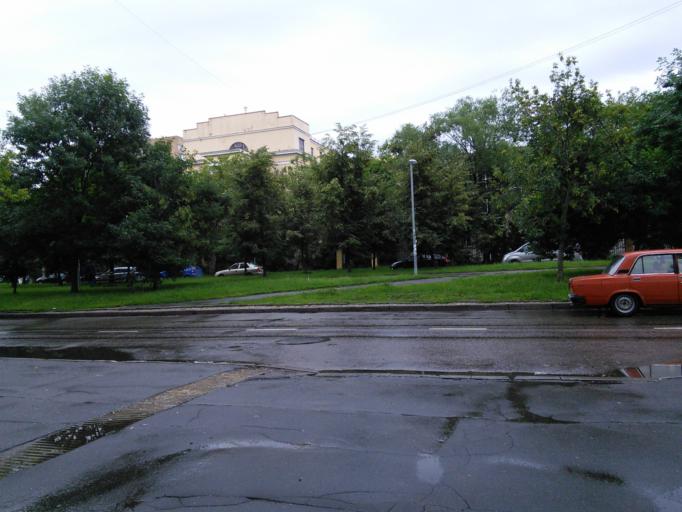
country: RU
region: Moskovskaya
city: Koptevo
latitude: 55.8378
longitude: 37.5312
